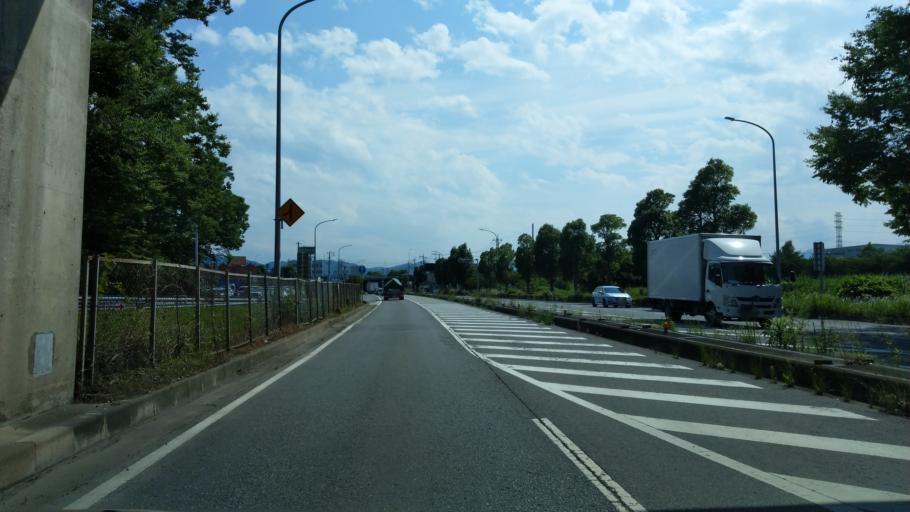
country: JP
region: Saitama
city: Honjo
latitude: 36.2232
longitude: 139.1648
